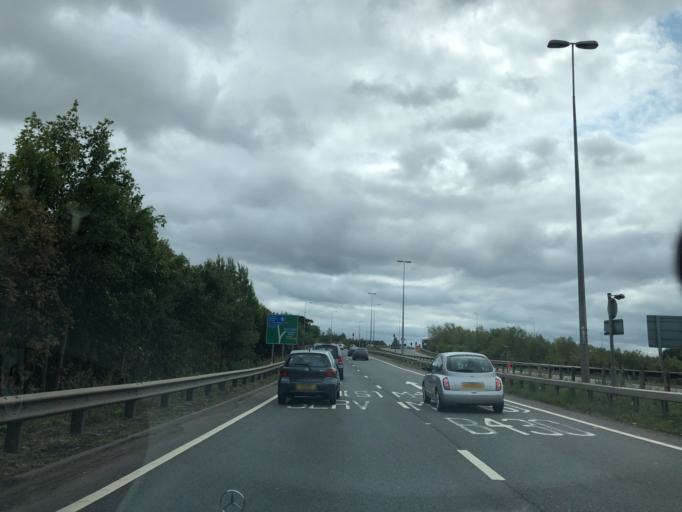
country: GB
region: England
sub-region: Oxfordshire
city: Bicester
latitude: 51.9510
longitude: -1.2043
